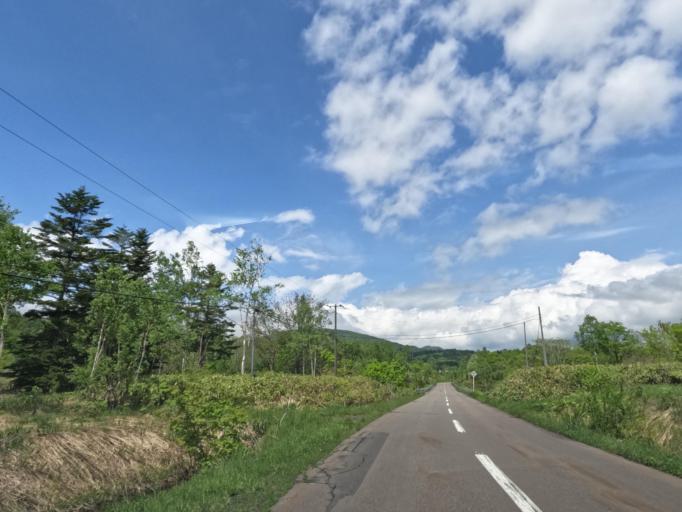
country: JP
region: Hokkaido
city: Tobetsu
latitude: 43.5247
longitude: 141.5877
